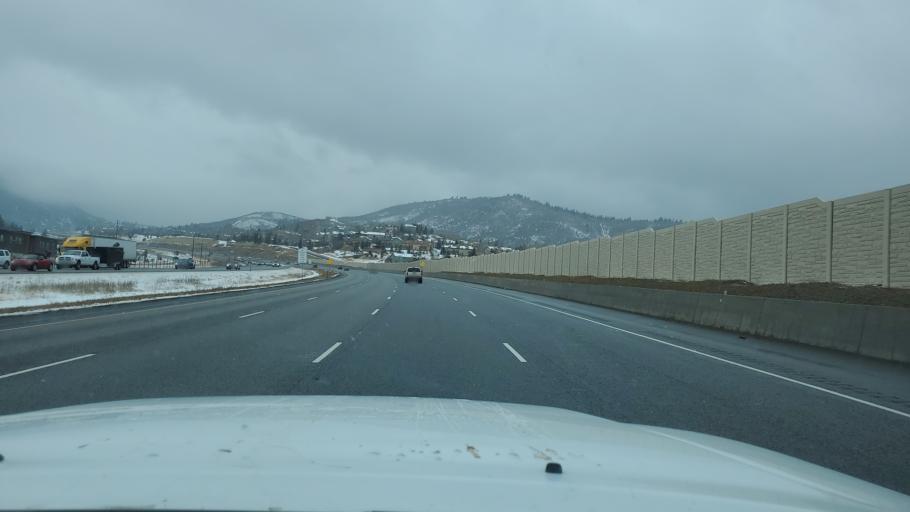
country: US
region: Utah
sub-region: Summit County
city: Summit Park
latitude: 40.7565
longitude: -111.5787
